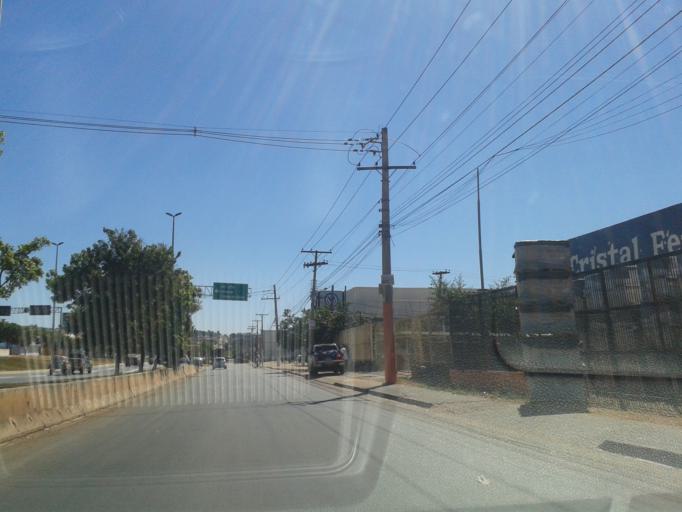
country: BR
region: Goias
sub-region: Goiania
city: Goiania
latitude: -16.6521
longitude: -49.3327
